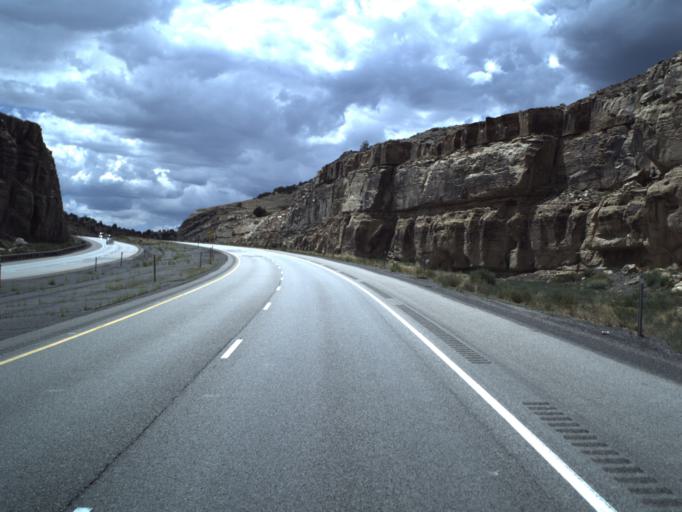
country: US
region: Utah
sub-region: Emery County
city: Ferron
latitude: 38.8049
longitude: -111.2635
